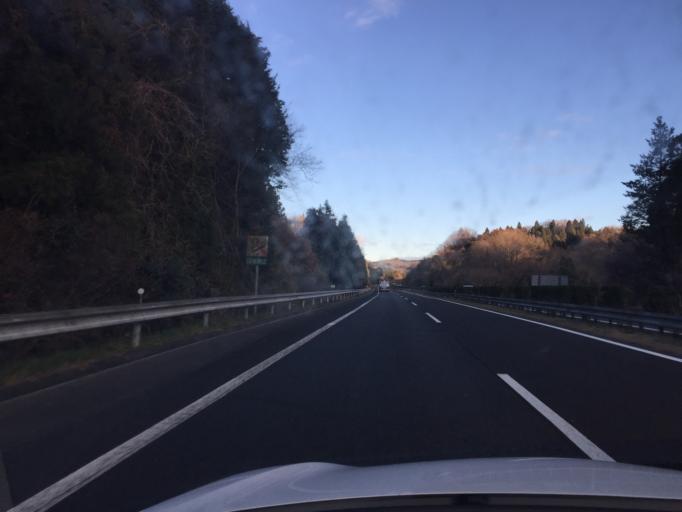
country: JP
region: Ibaraki
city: Kitaibaraki
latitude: 36.8150
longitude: 140.7306
